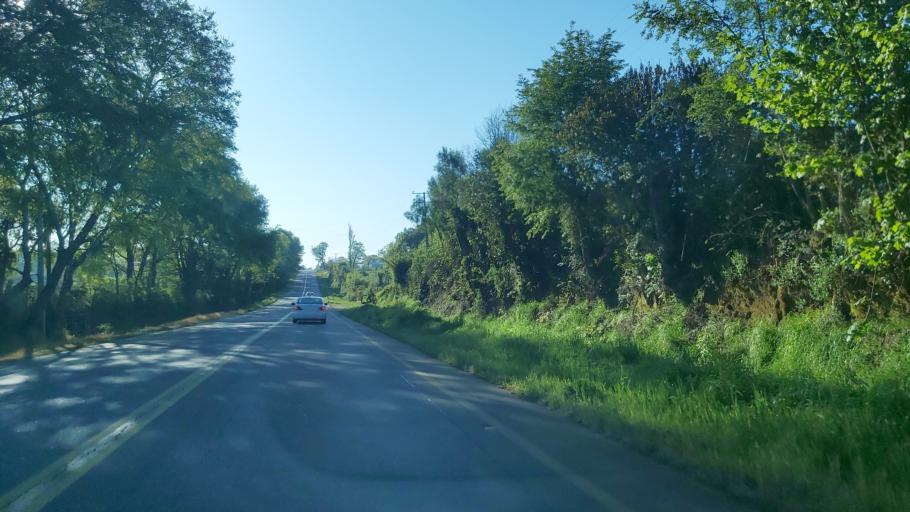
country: CL
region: Araucania
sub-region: Provincia de Malleco
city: Victoria
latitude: -38.2626
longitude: -72.2423
